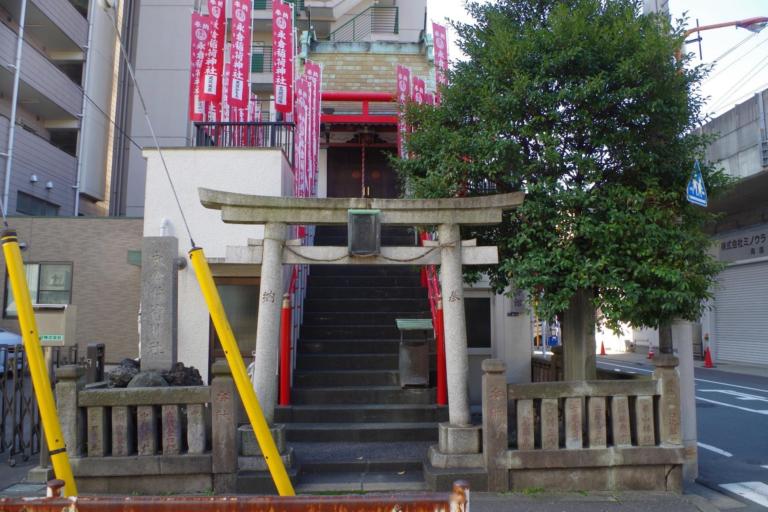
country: JP
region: Tokyo
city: Urayasu
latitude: 35.6961
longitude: 139.8066
